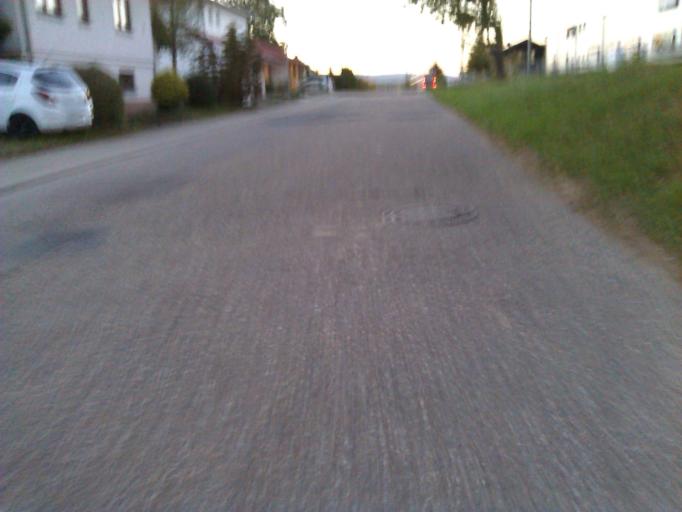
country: DE
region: Baden-Wuerttemberg
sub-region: Karlsruhe Region
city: Zuzenhausen
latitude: 49.2974
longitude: 8.8212
